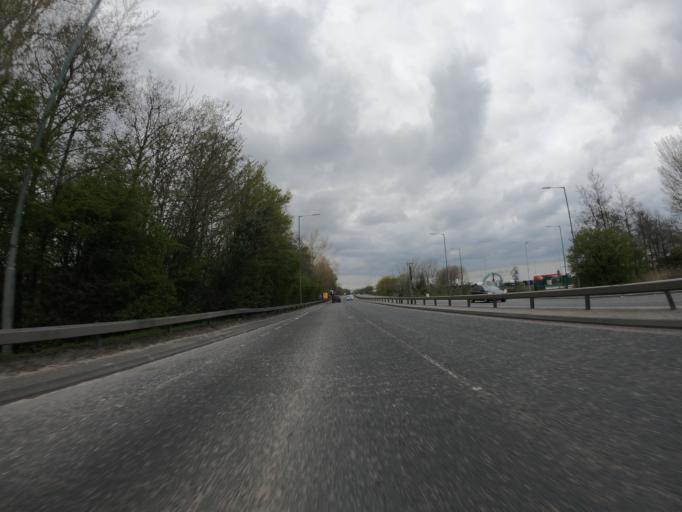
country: GB
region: England
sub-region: Greater London
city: Belvedere
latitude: 51.4917
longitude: 0.1636
